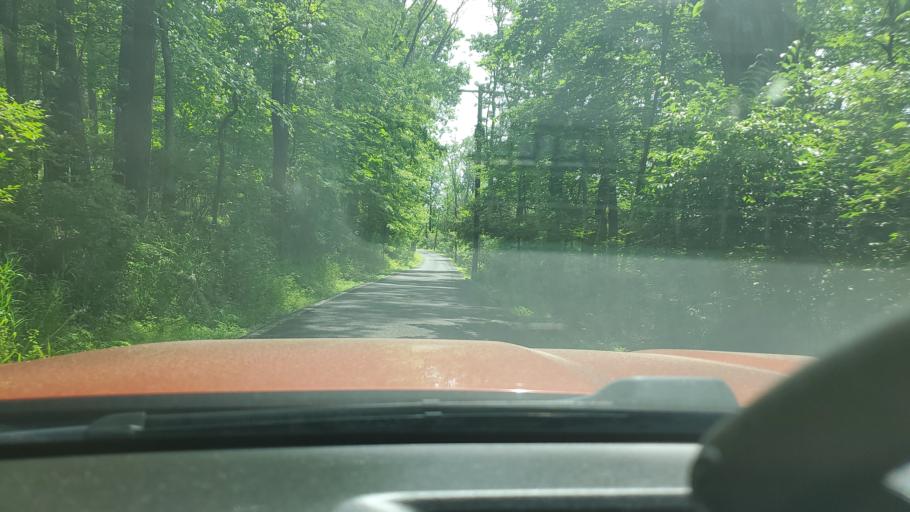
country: US
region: Pennsylvania
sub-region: Montgomery County
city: Schwenksville
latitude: 40.2743
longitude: -75.5012
